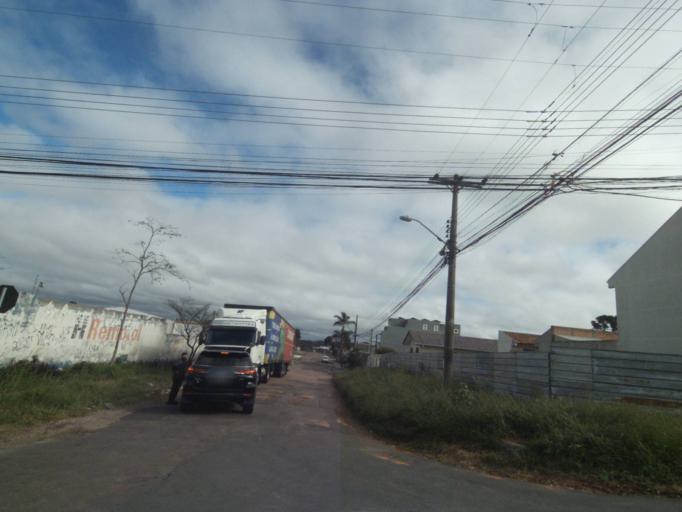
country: BR
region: Parana
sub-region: Sao Jose Dos Pinhais
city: Sao Jose dos Pinhais
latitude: -25.5248
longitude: -49.2990
